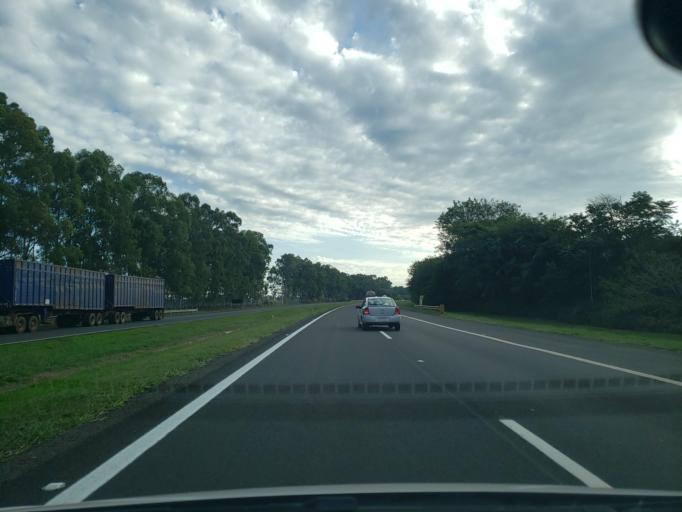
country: BR
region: Sao Paulo
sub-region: Guararapes
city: Guararapes
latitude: -21.2147
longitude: -50.6885
